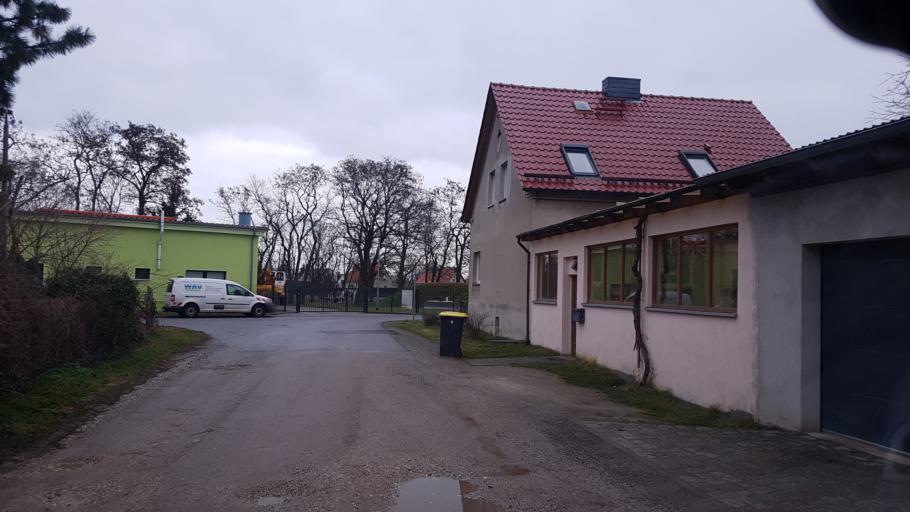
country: DE
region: Brandenburg
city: Doberlug-Kirchhain
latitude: 51.6069
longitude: 13.5584
